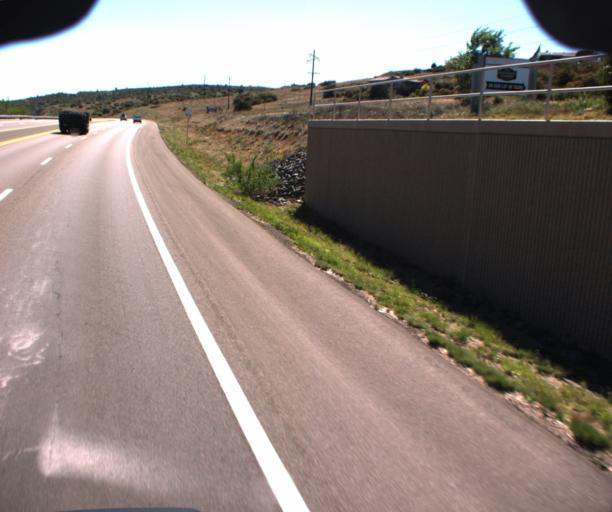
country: US
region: Arizona
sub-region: Yavapai County
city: Prescott
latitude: 34.5718
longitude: -112.4376
